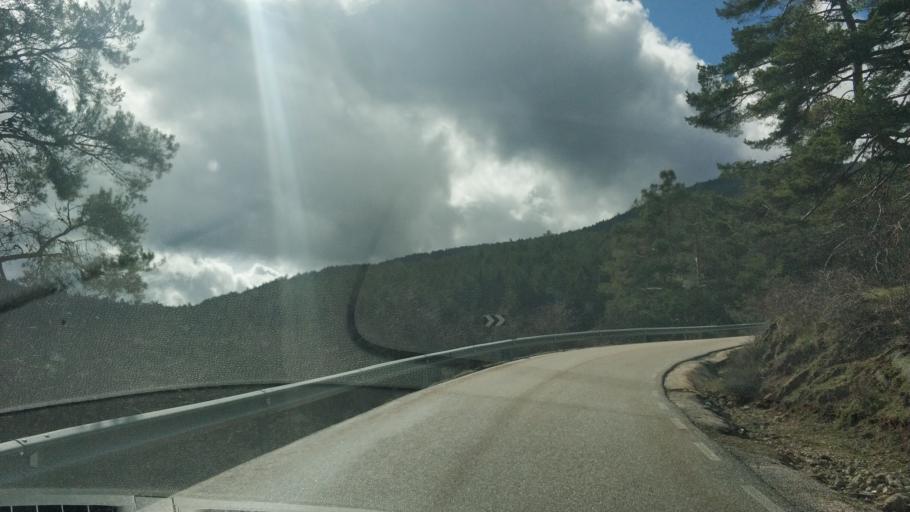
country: ES
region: Castille and Leon
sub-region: Provincia de Burgos
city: Neila
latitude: 42.0543
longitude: -3.0099
